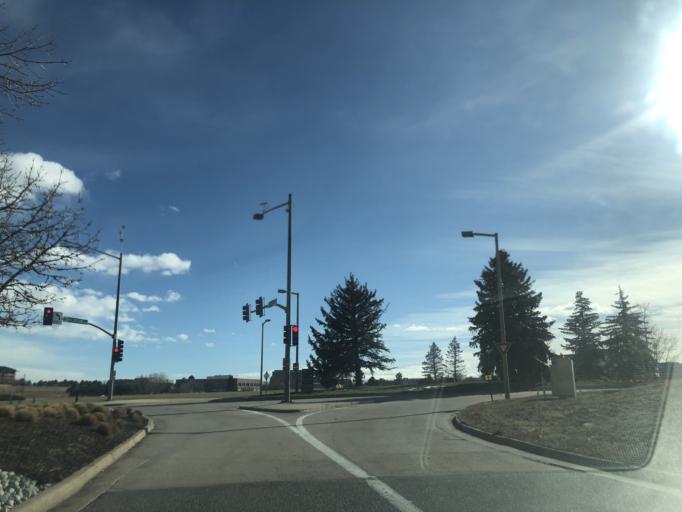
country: US
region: Colorado
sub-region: Douglas County
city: Meridian
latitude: 39.5460
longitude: -104.8648
